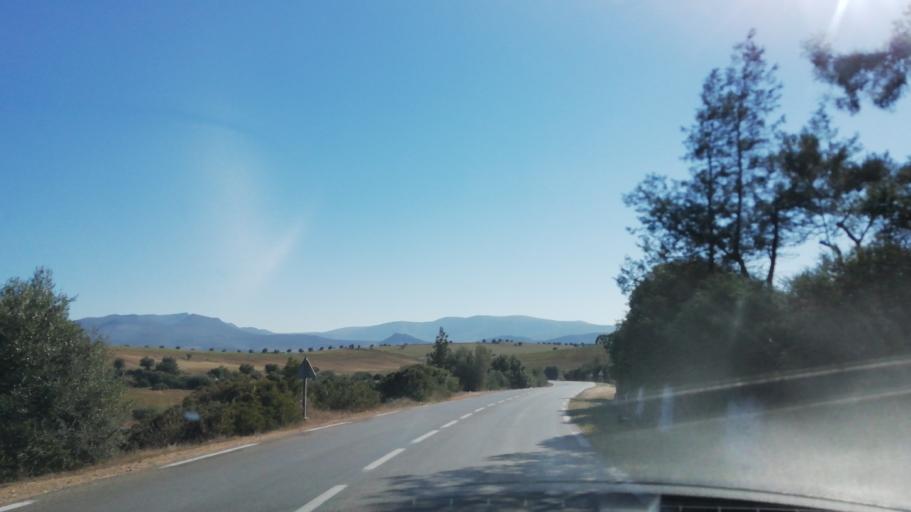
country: DZ
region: Tlemcen
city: Beni Mester
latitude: 34.8272
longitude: -1.5867
